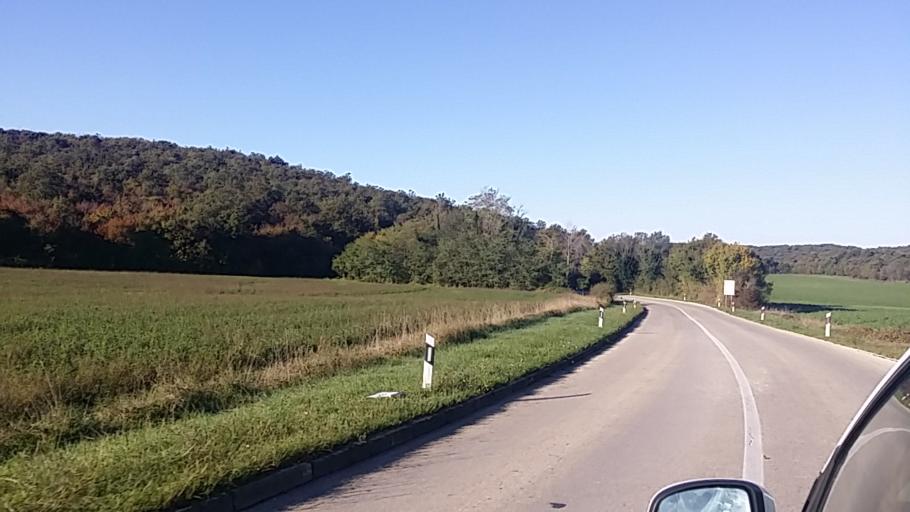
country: HR
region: Istarska
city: Vrsar
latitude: 45.1537
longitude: 13.6502
